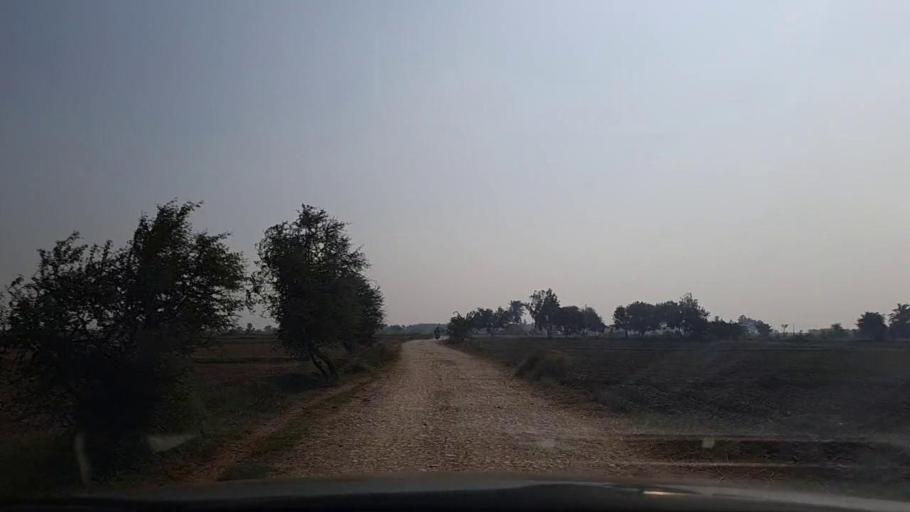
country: PK
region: Sindh
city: Mirpur Sakro
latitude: 24.5672
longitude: 67.7769
